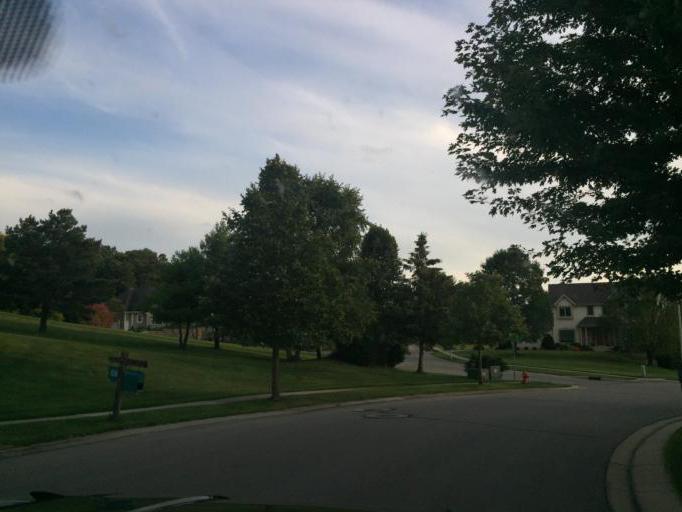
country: US
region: Minnesota
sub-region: Olmsted County
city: Rochester
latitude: 44.0124
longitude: -92.5048
